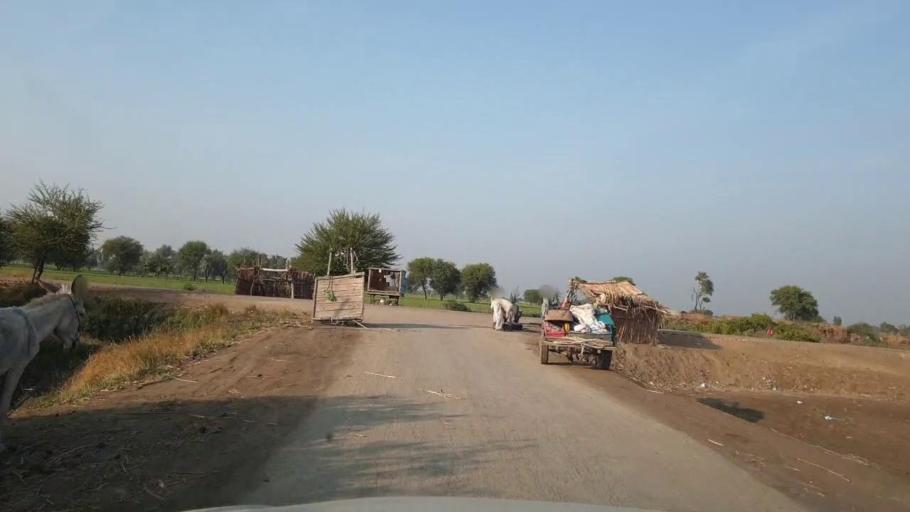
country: PK
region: Sindh
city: Pithoro
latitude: 25.6761
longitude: 69.2045
